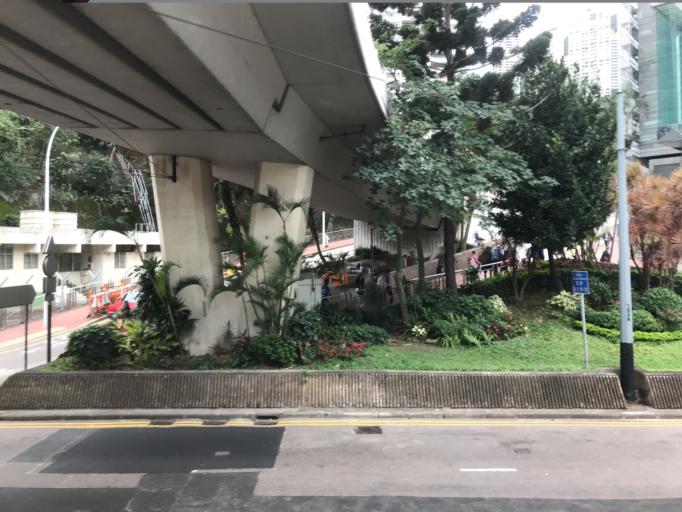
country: HK
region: Wanchai
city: Wan Chai
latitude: 22.2777
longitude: 114.1668
